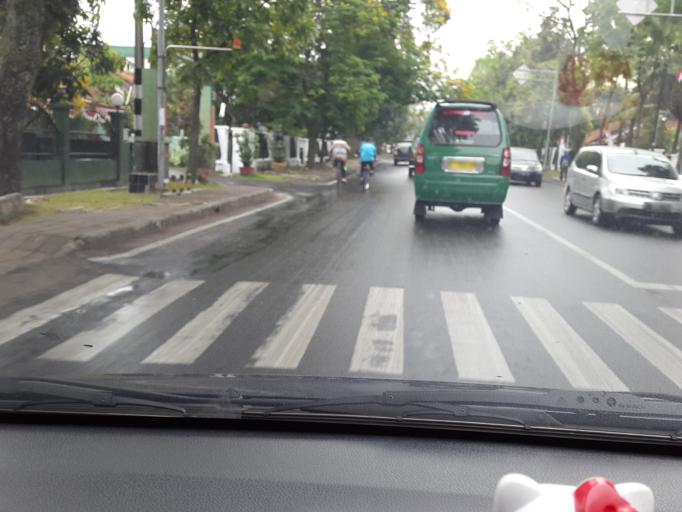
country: ID
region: West Java
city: Bandung
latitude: -6.9018
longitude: 107.6349
